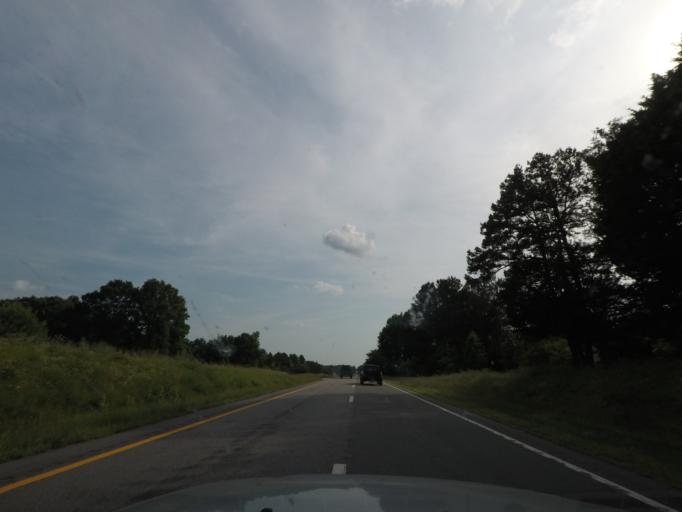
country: US
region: Virginia
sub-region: Mecklenburg County
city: Chase City
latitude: 36.8933
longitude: -78.5464
